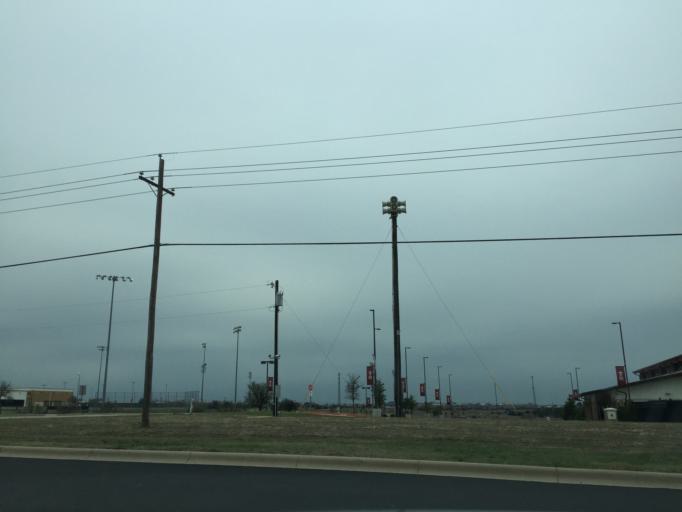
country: US
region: Texas
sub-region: Bell County
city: Fort Hood
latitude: 31.1168
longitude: -97.8083
